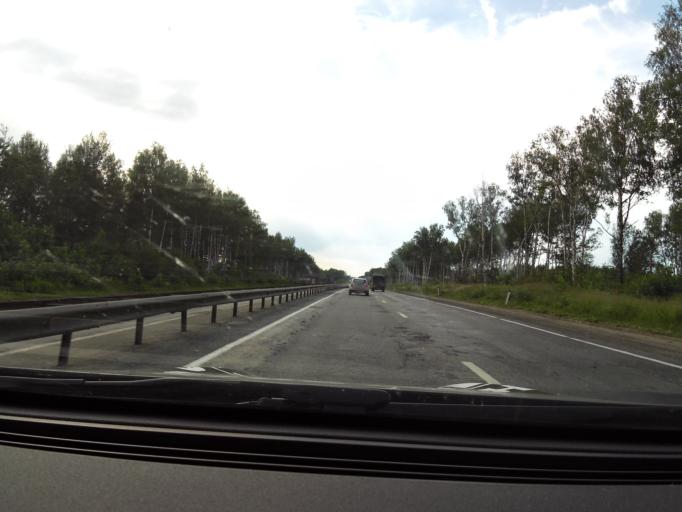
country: RU
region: Vladimir
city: Novovyazniki
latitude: 56.2064
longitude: 42.2822
